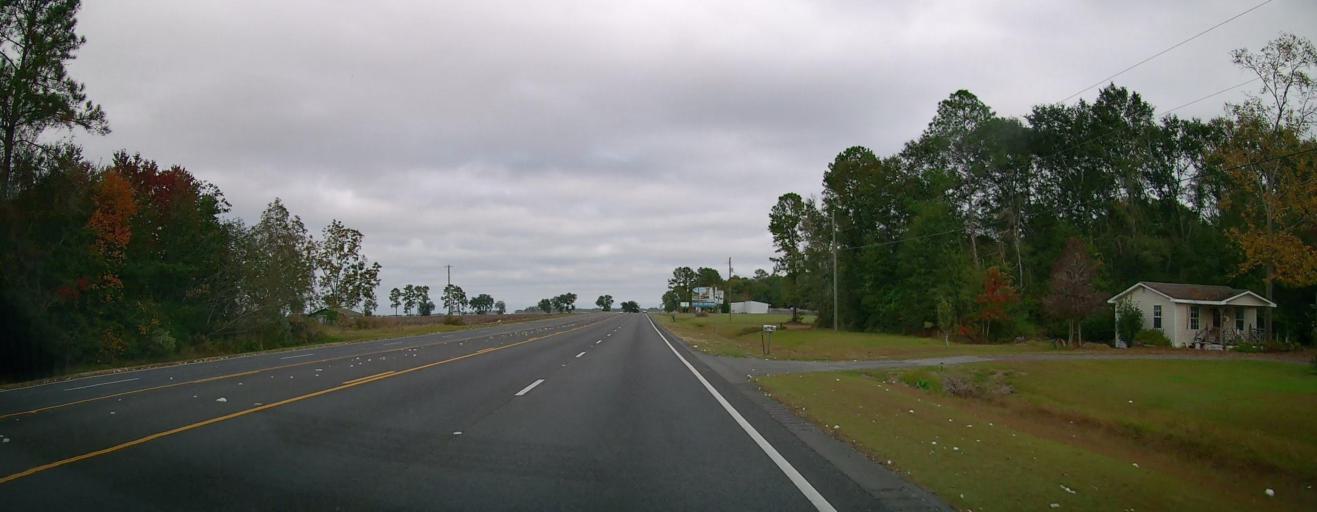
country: US
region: Georgia
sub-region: Colquitt County
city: Moultrie
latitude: 31.0222
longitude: -83.8632
